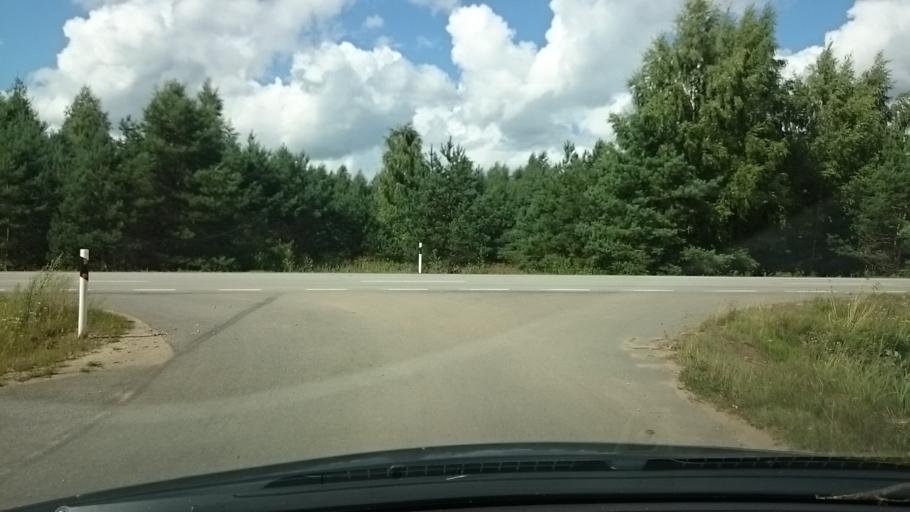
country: EE
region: Vorumaa
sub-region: Voru linn
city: Voru
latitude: 57.9169
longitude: 27.1798
